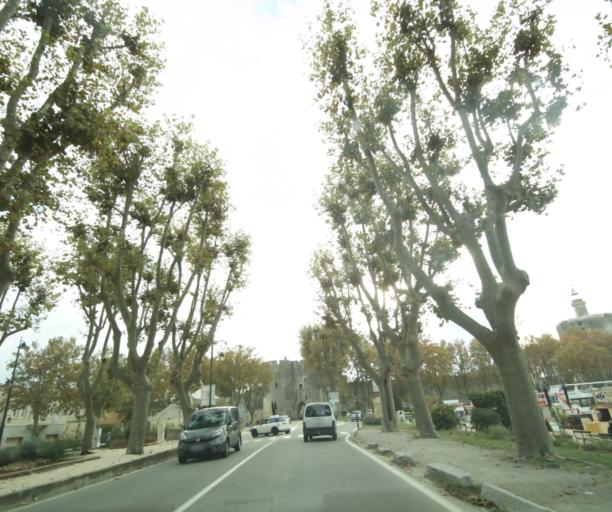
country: FR
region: Languedoc-Roussillon
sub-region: Departement du Gard
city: Aigues-Mortes
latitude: 43.5692
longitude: 4.1918
